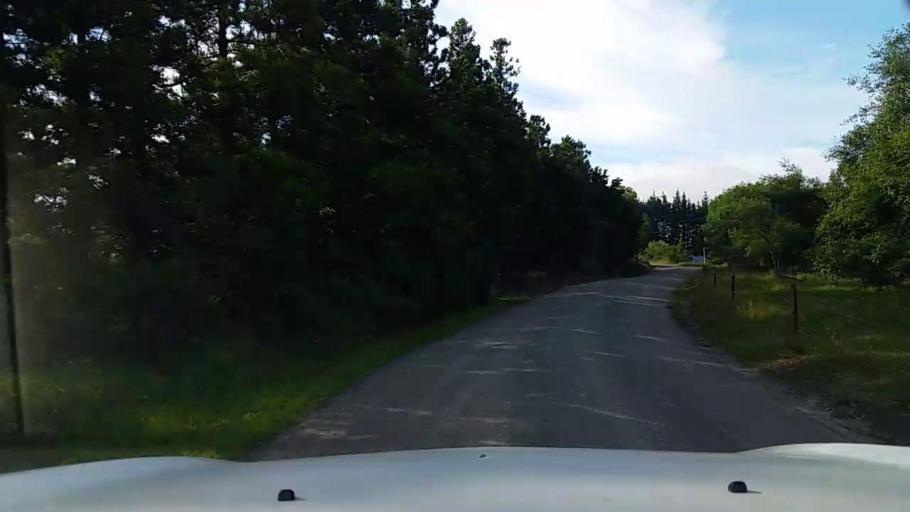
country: NZ
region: Northland
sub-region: Whangarei
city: Maungatapere
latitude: -35.6784
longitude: 174.1786
